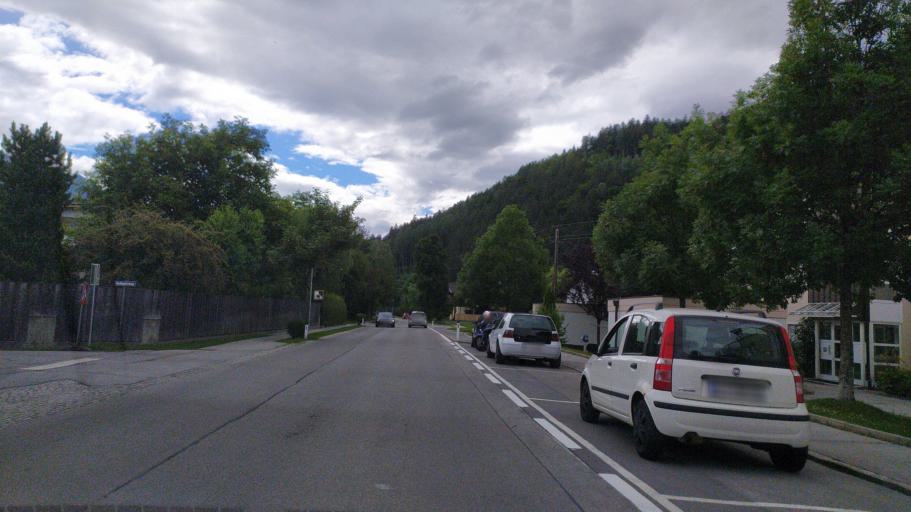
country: AT
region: Tyrol
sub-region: Politischer Bezirk Lienz
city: Tristach
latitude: 46.8160
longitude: 12.7984
